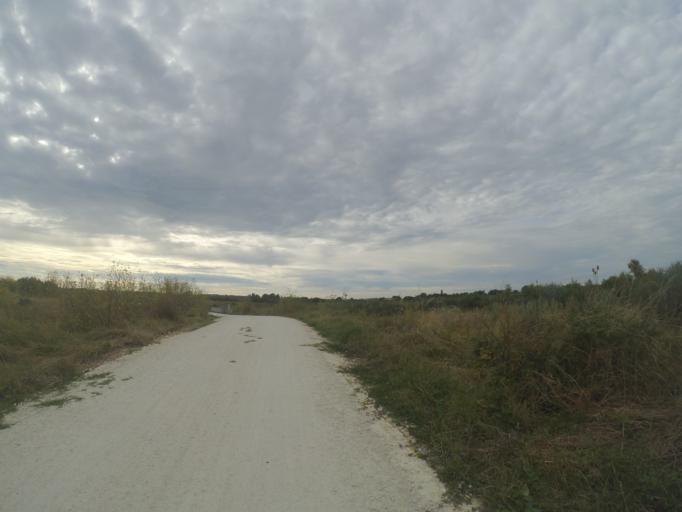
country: FR
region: Poitou-Charentes
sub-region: Departement de la Charente-Maritime
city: Meschers-sur-Gironde
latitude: 45.5576
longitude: -0.9328
